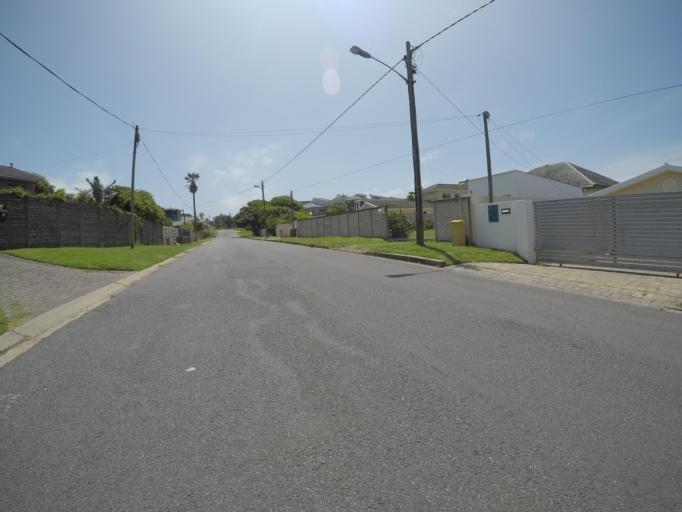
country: ZA
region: Eastern Cape
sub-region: Buffalo City Metropolitan Municipality
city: East London
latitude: -32.9423
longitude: 28.0285
